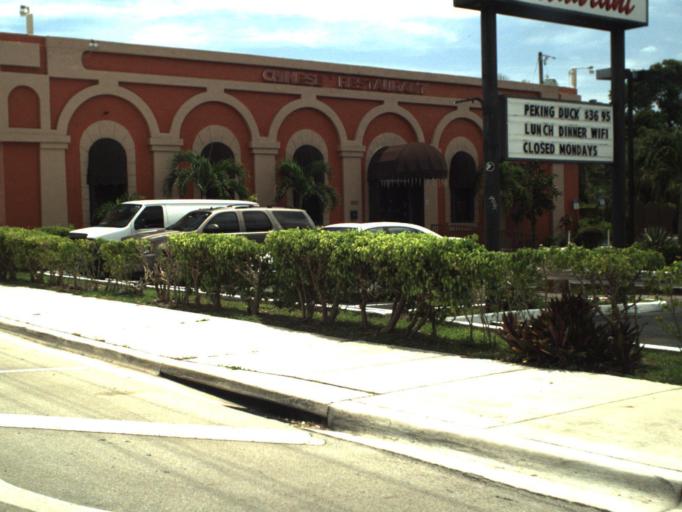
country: US
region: Florida
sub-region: Broward County
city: Pompano Beach
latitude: 26.2316
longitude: -80.1115
